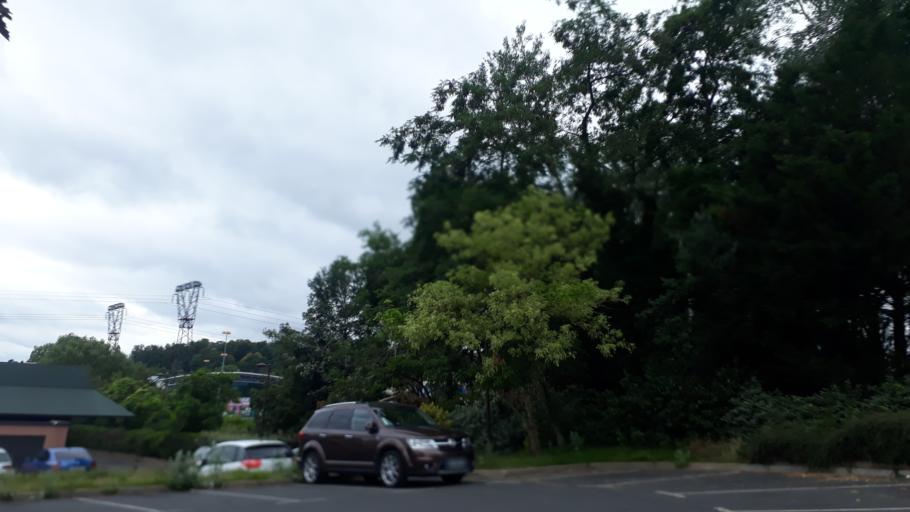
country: FR
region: Ile-de-France
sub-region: Departement de l'Essonne
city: La Ville-du-Bois
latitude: 48.6715
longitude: 2.2768
